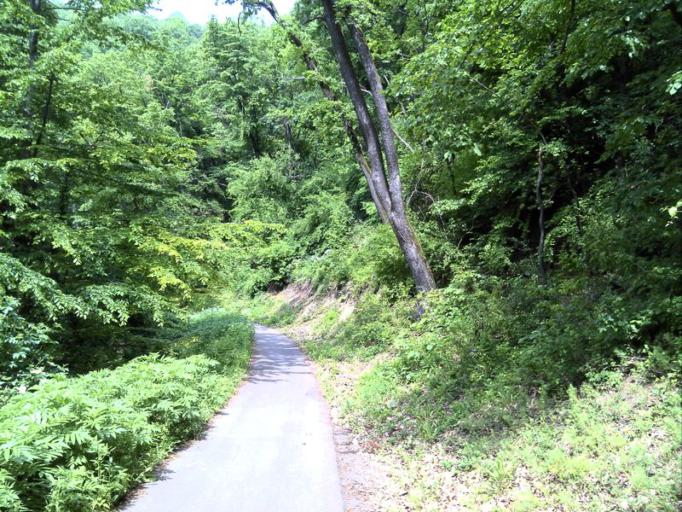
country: HU
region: Baranya
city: Pecs
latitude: 46.1102
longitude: 18.1804
